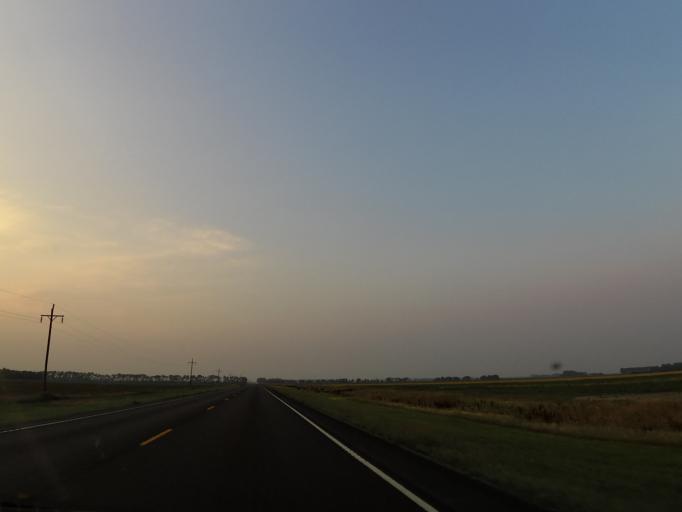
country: US
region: North Dakota
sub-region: Walsh County
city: Park River
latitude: 48.3477
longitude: -97.6224
